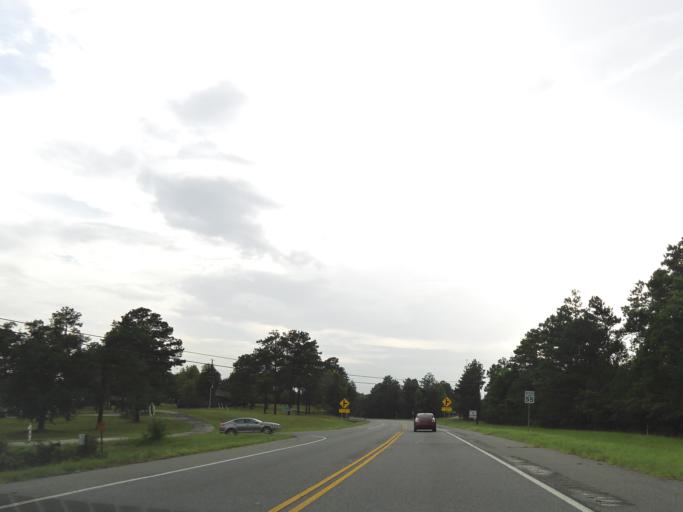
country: US
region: Georgia
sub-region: Bibb County
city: West Point
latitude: 32.8090
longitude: -83.8298
